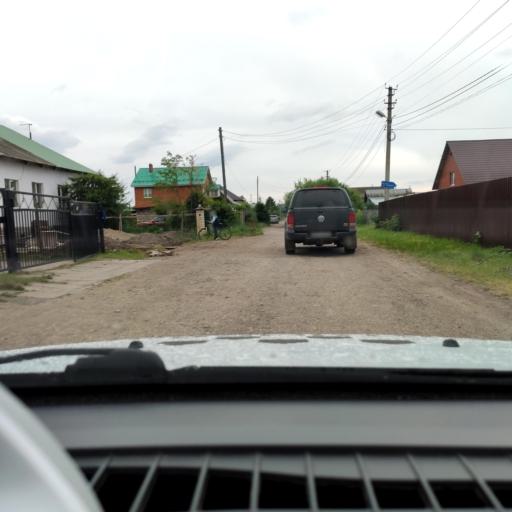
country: RU
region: Perm
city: Froly
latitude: 57.9160
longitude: 56.2754
